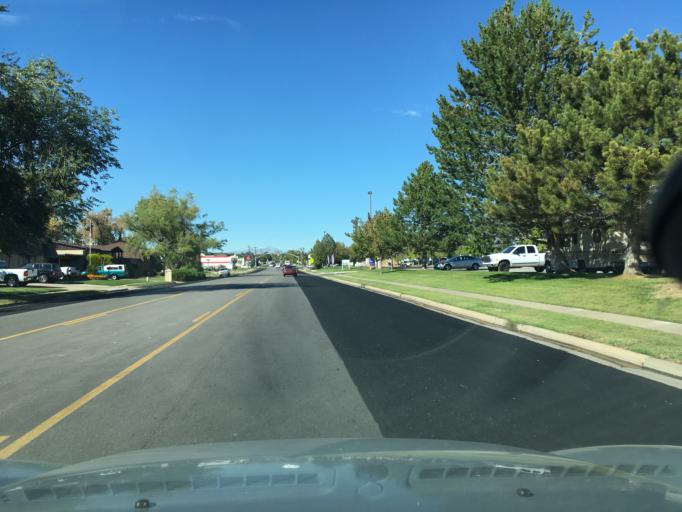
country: US
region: Utah
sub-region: Davis County
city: Layton
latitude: 41.0717
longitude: -111.9501
